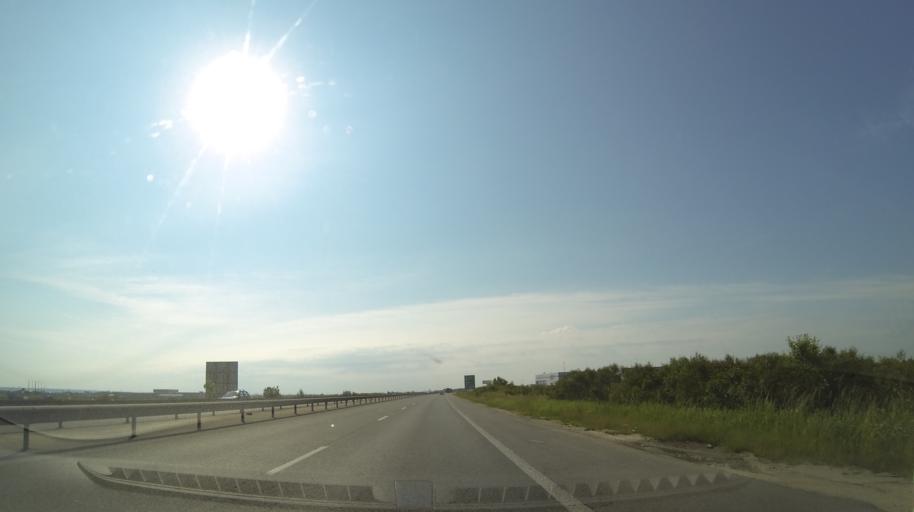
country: RO
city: Oarja Sat
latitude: 44.7953
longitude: 24.9816
